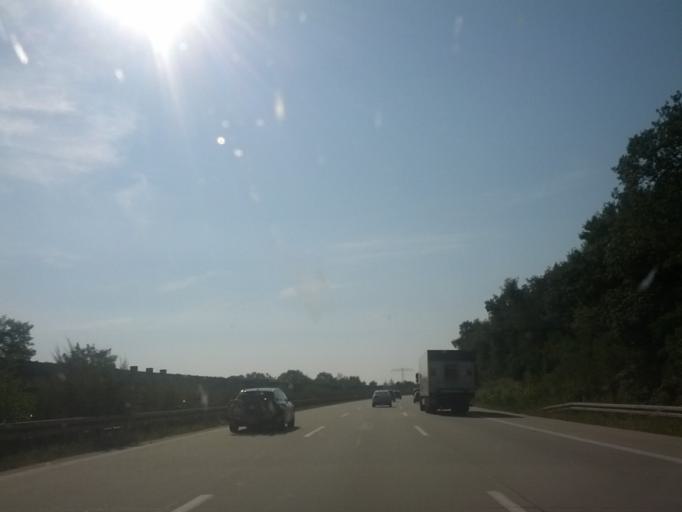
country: DE
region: Brandenburg
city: Woltersdorf
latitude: 52.4609
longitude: 13.7944
